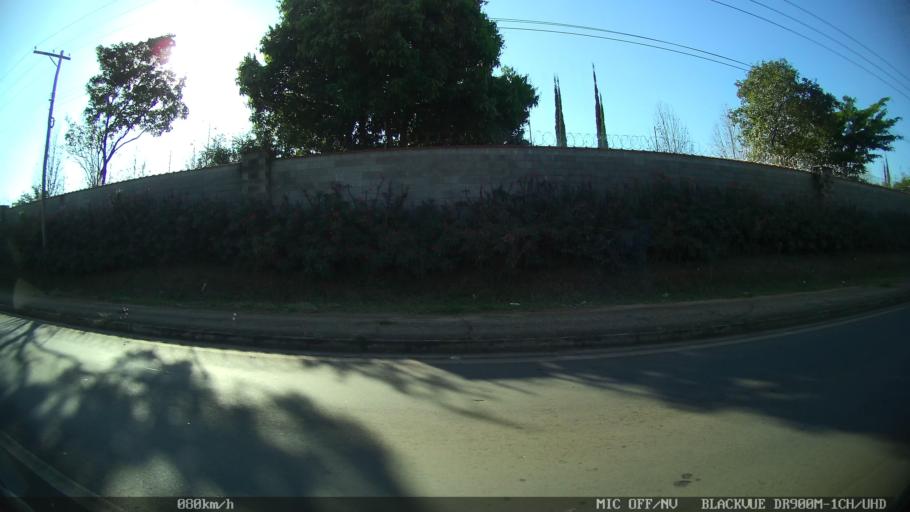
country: BR
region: Sao Paulo
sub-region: Nova Odessa
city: Nova Odessa
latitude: -22.7672
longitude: -47.2713
